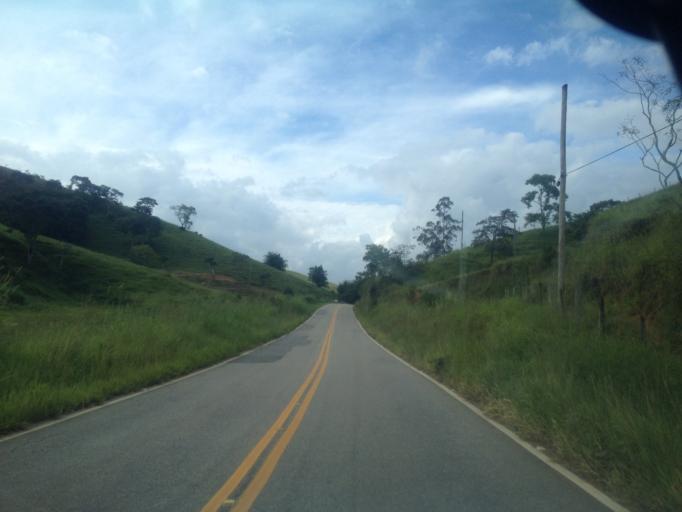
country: BR
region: Rio de Janeiro
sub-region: Quatis
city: Quatis
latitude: -22.3569
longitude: -44.2530
